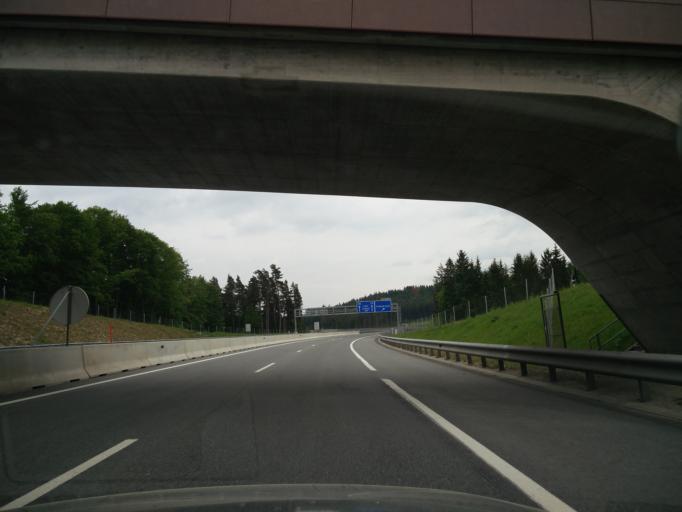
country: AT
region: Upper Austria
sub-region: Politischer Bezirk Freistadt
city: Freistadt
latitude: 48.5217
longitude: 14.5114
